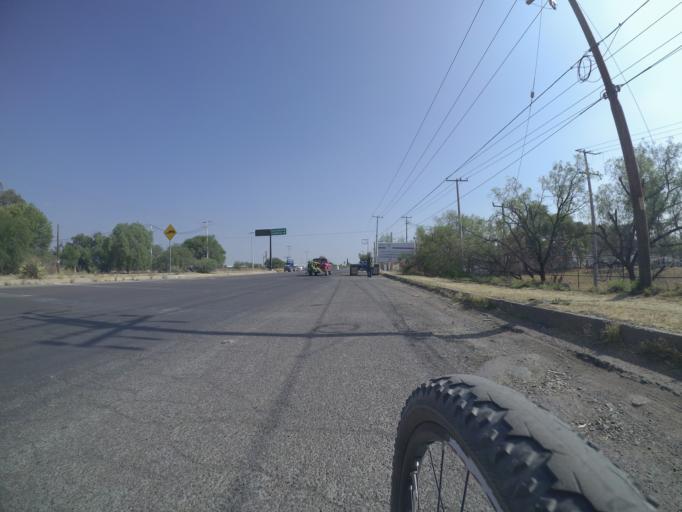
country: MX
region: Aguascalientes
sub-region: Jesus Maria
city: Paseos de las Haciendas [Fraccionamiento]
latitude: 21.9958
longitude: -102.3324
